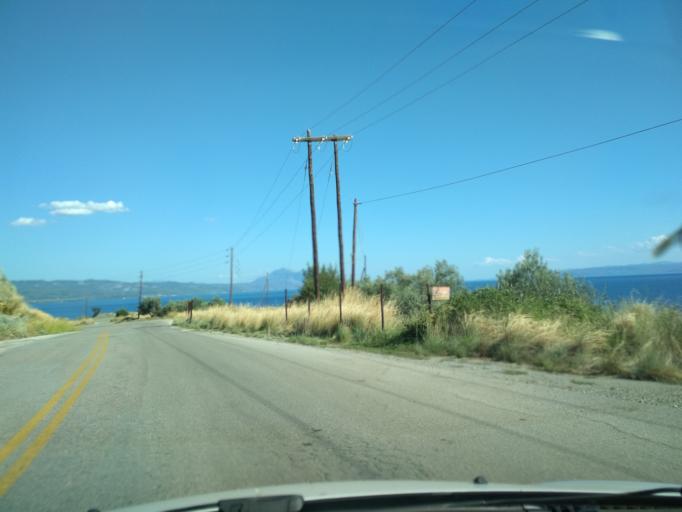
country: GR
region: Central Greece
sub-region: Nomos Evvoias
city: Oreoi
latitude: 38.8418
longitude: 23.0977
